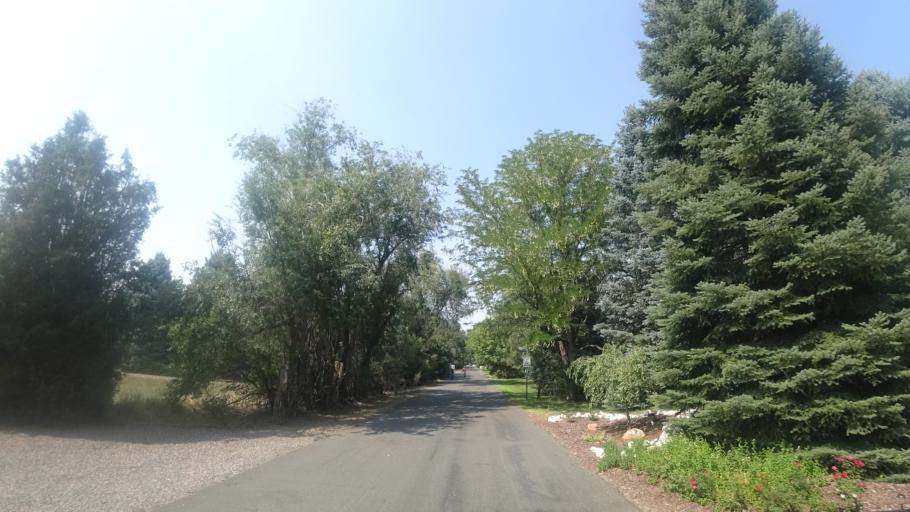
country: US
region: Colorado
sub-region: Arapahoe County
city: Cherry Hills Village
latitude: 39.6357
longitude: -104.9715
